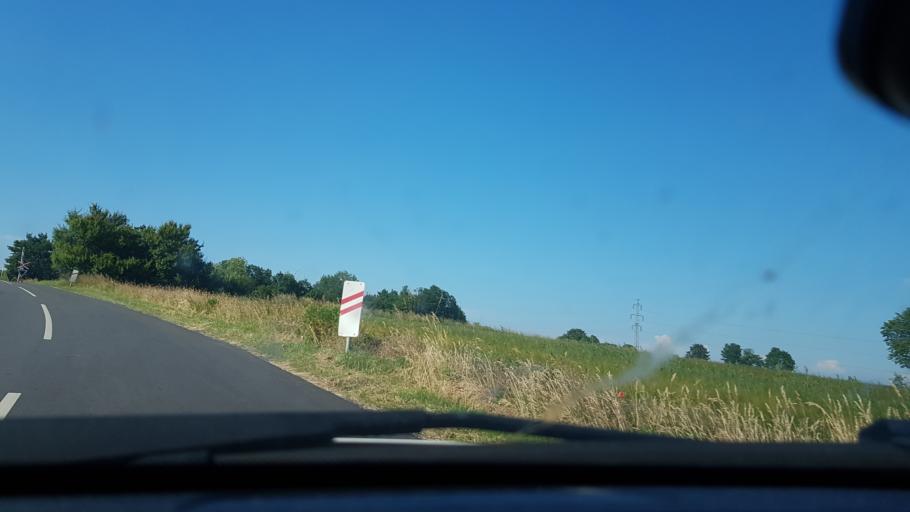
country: DK
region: Zealand
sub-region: Odsherred Kommune
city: Hojby
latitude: 55.8638
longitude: 11.5985
